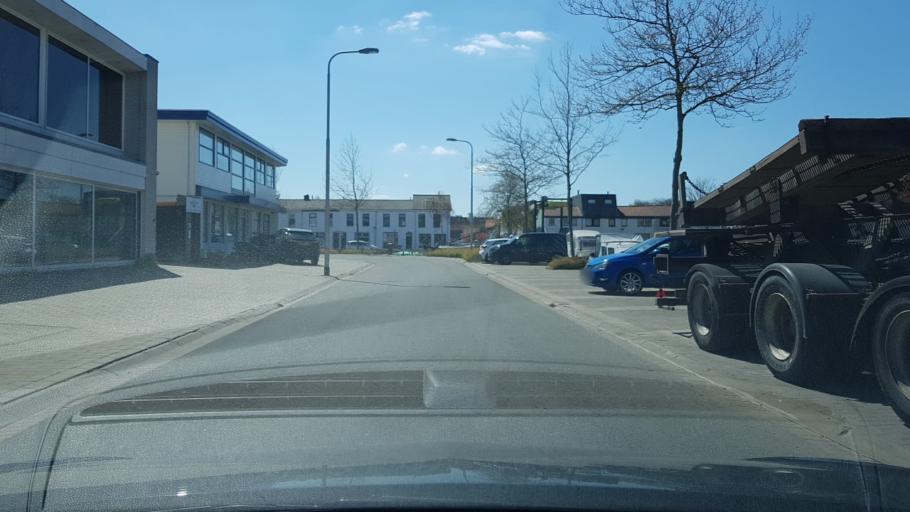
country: NL
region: South Holland
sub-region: Gemeente Hillegom
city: Hillegom
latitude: 52.2901
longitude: 4.5827
